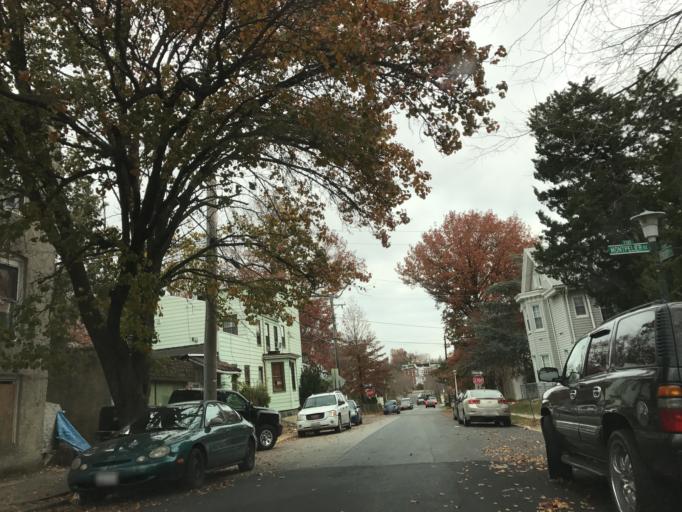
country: US
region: Maryland
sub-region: City of Baltimore
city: Baltimore
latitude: 39.3261
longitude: -76.6073
